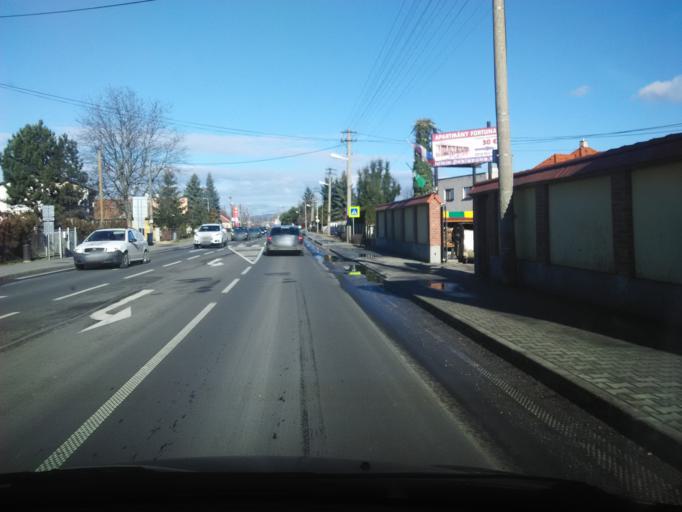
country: SK
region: Nitriansky
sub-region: Okres Nitra
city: Nitra
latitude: 48.2498
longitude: 18.1106
